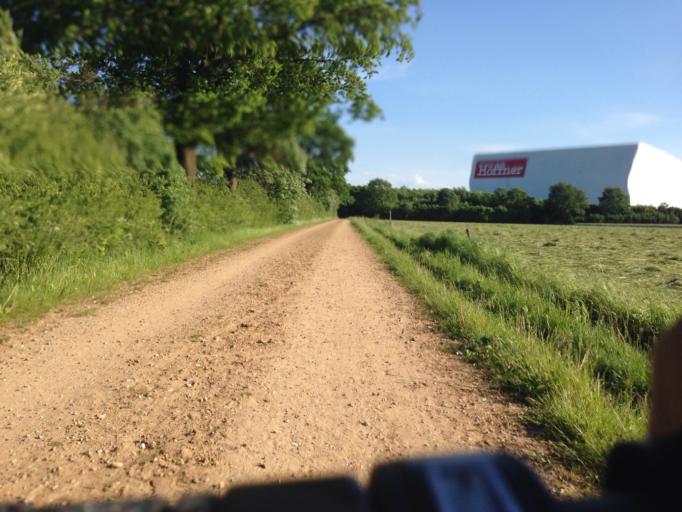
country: DE
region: Schleswig-Holstein
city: Stapelfeld
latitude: 53.5828
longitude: 10.2022
